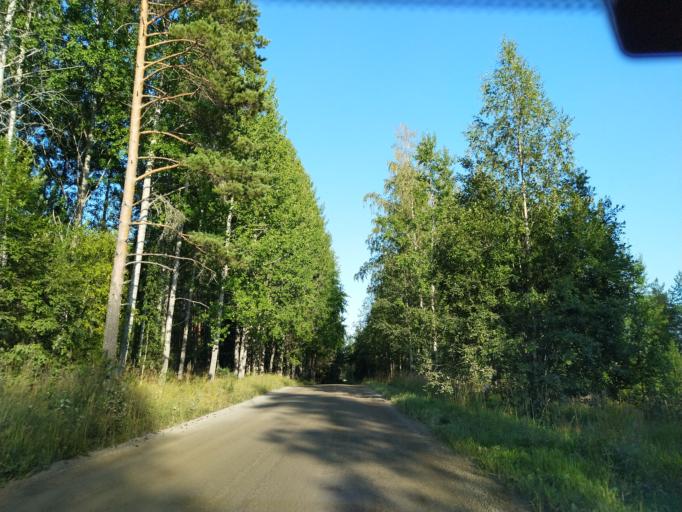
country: FI
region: Central Finland
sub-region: Jaemsae
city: Kuhmoinen
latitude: 61.6031
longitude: 25.1464
